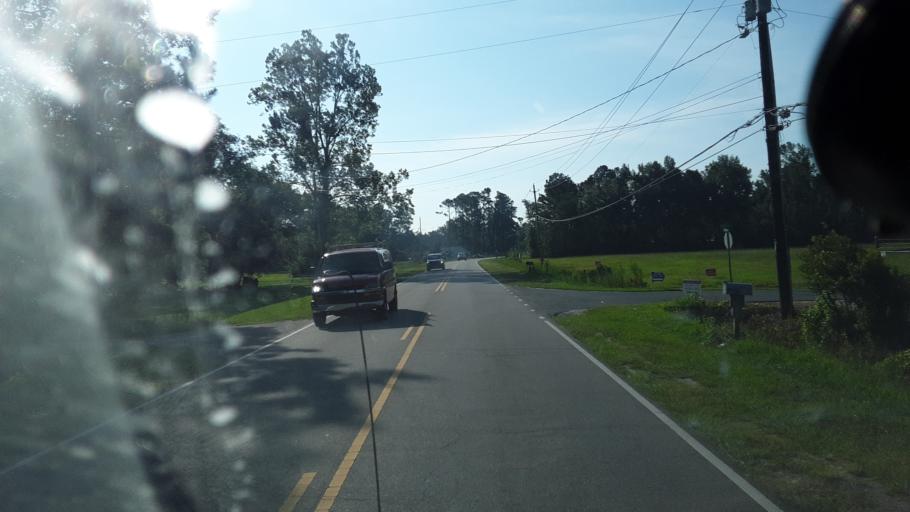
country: US
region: North Carolina
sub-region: Brunswick County
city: Leland
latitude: 34.2537
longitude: -78.0399
